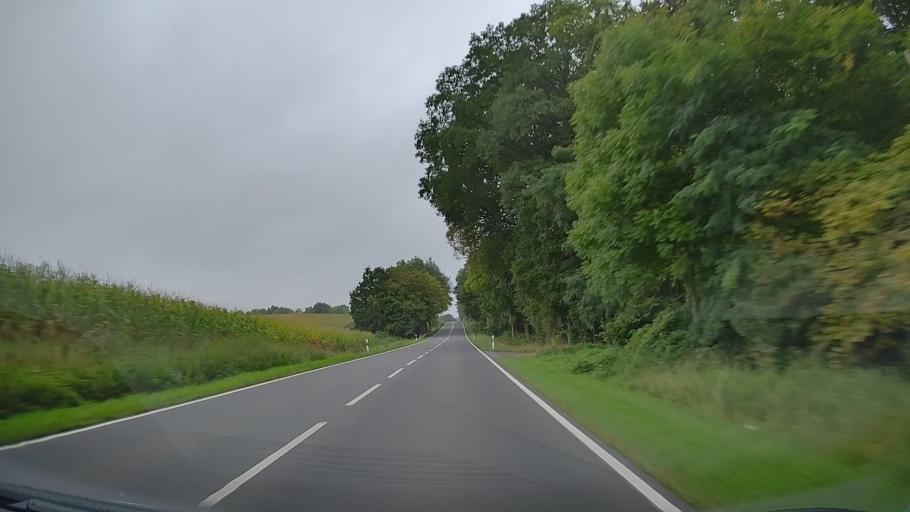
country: DE
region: Mecklenburg-Vorpommern
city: Tarnow
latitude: 53.7435
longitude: 12.0123
